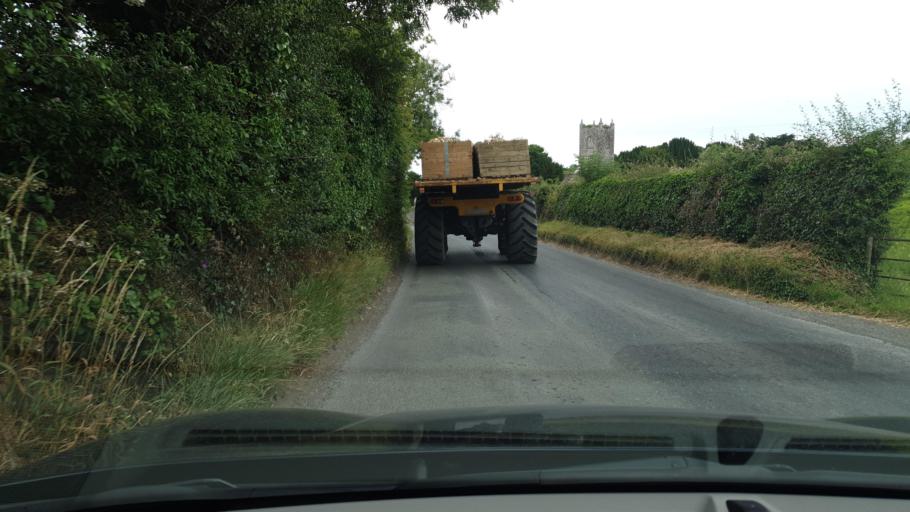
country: IE
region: Leinster
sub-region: An Mhi
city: Ashbourne
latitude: 53.5692
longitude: -6.3859
